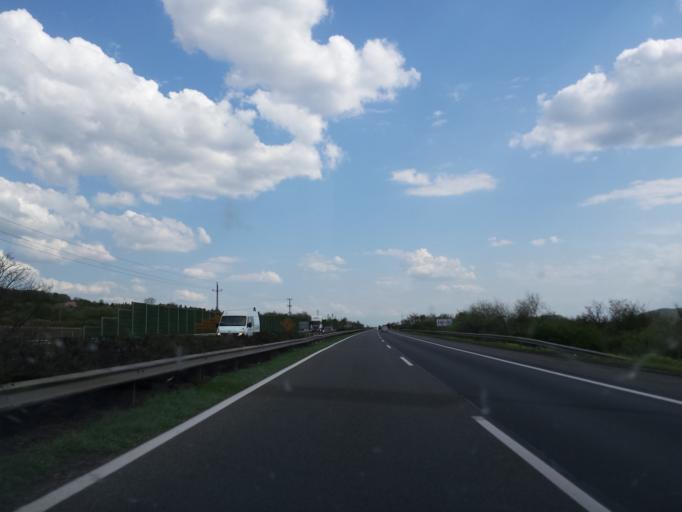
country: HU
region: Pest
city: Biatorbagy
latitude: 47.4892
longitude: 18.8301
